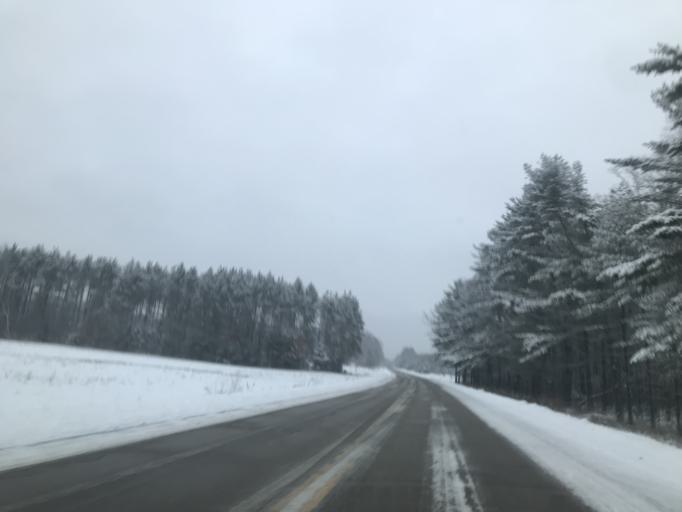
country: US
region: Wisconsin
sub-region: Oconto County
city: Oconto Falls
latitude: 44.8616
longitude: -88.1096
